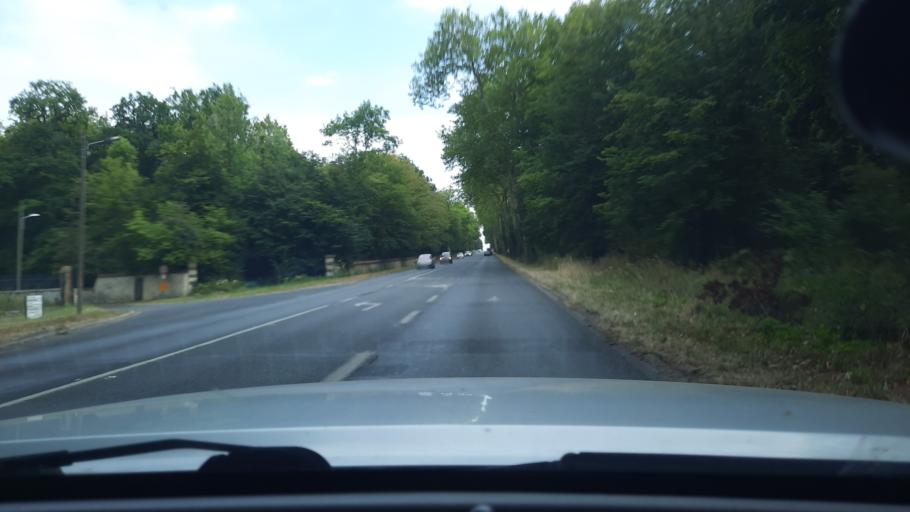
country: FR
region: Ile-de-France
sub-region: Departement de Seine-et-Marne
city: La Rochette
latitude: 48.5126
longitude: 2.6567
